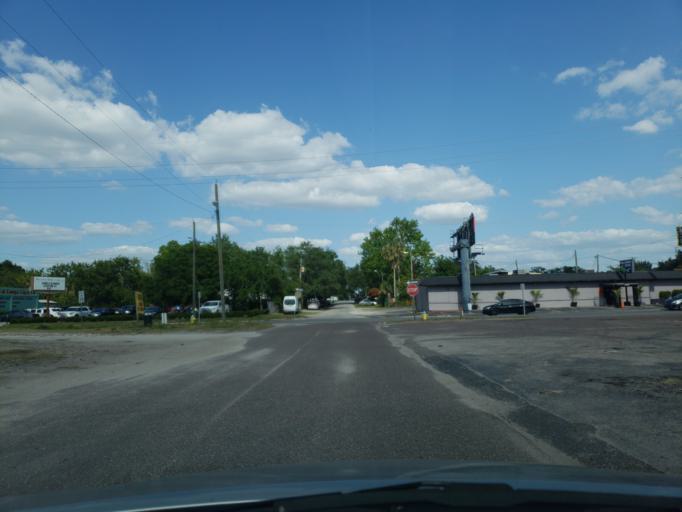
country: US
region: Florida
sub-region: Hillsborough County
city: Tampa
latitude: 27.9674
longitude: -82.4833
